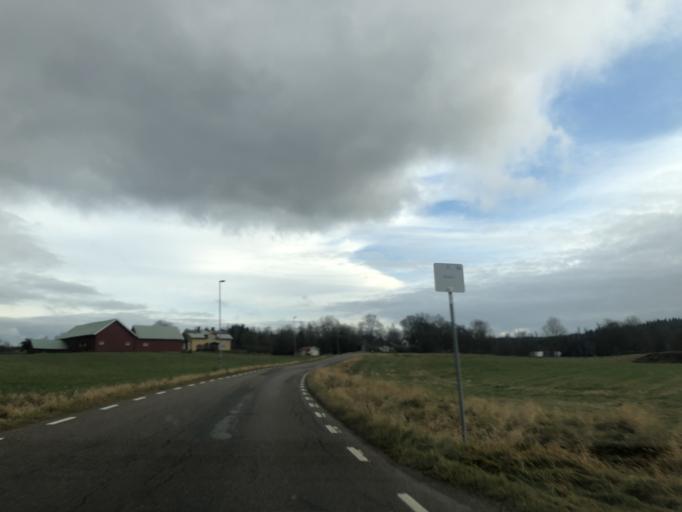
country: SE
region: Vaestra Goetaland
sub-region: Boras Kommun
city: Dalsjofors
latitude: 57.8295
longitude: 13.1730
